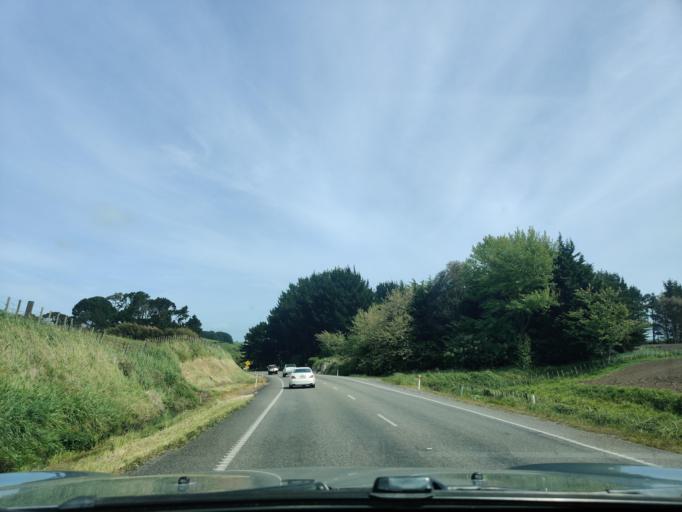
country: NZ
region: Taranaki
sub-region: South Taranaki District
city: Hawera
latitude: -39.6331
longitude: 174.3772
